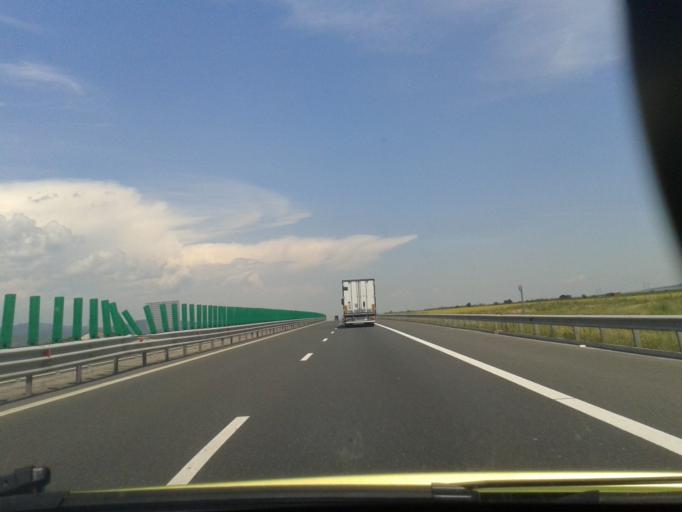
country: RO
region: Alba
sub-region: Oras Cugir
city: Vinerea
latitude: 45.8992
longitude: 23.2954
